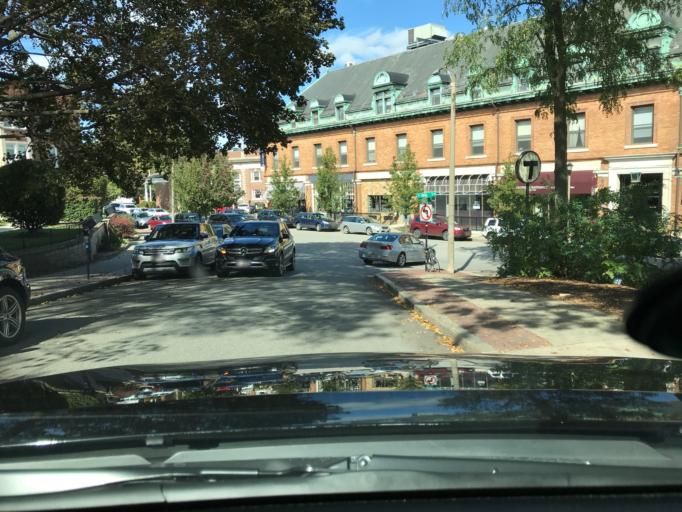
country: US
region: Massachusetts
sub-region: Middlesex County
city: Newton
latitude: 42.3292
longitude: -71.1934
